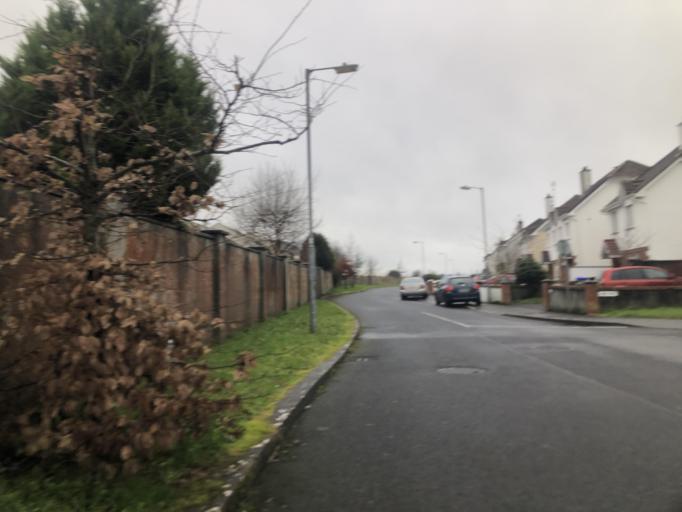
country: IE
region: Connaught
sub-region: County Galway
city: Tuam
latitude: 53.5112
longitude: -8.8716
